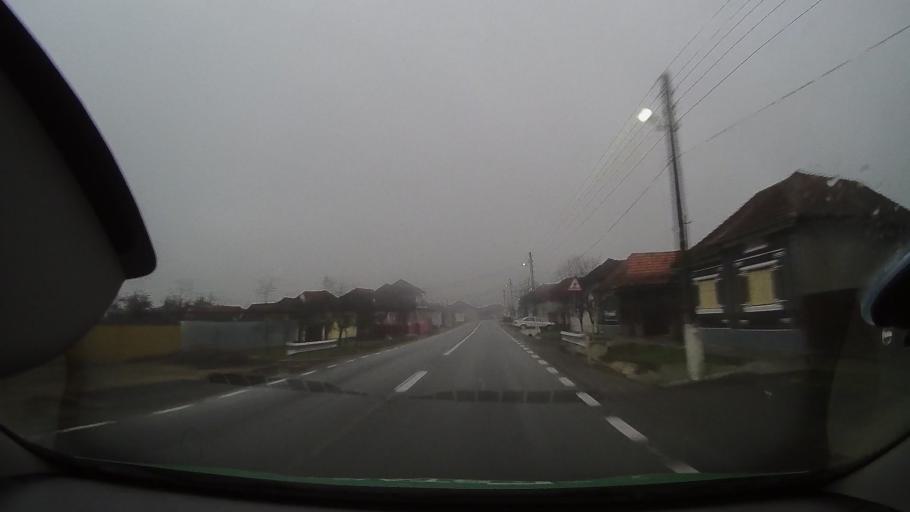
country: RO
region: Arad
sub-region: Comuna Craiova
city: Craiova
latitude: 46.6316
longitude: 21.9584
